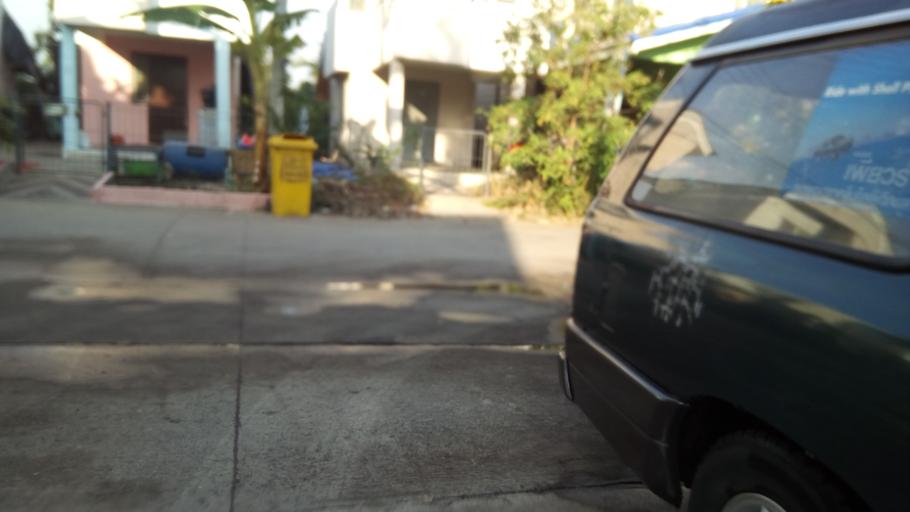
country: TH
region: Pathum Thani
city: Ban Rangsit
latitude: 14.0462
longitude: 100.8401
